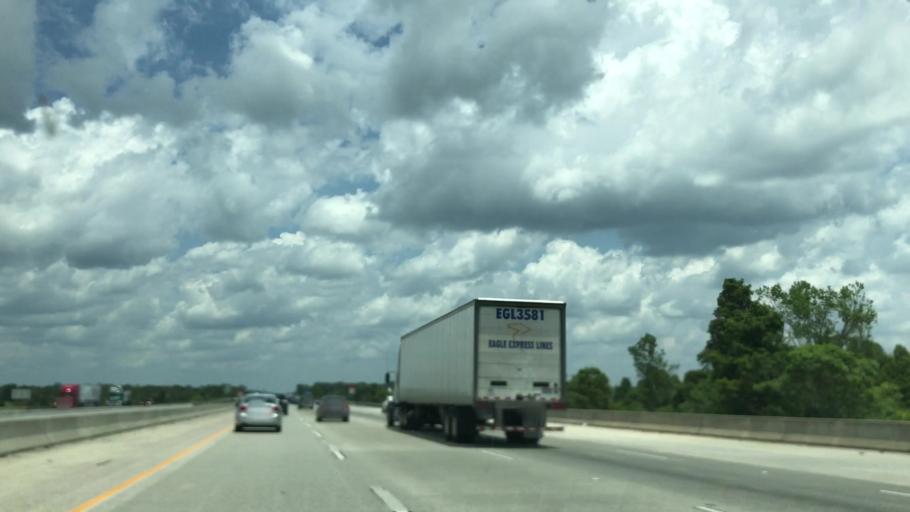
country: US
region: Georgia
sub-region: McIntosh County
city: Darien
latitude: 31.3551
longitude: -81.4599
